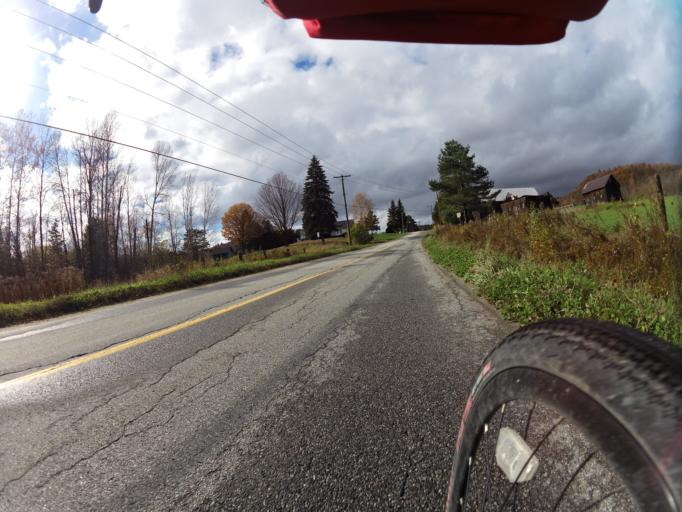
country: CA
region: Quebec
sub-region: Outaouais
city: Wakefield
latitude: 45.6948
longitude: -76.0109
